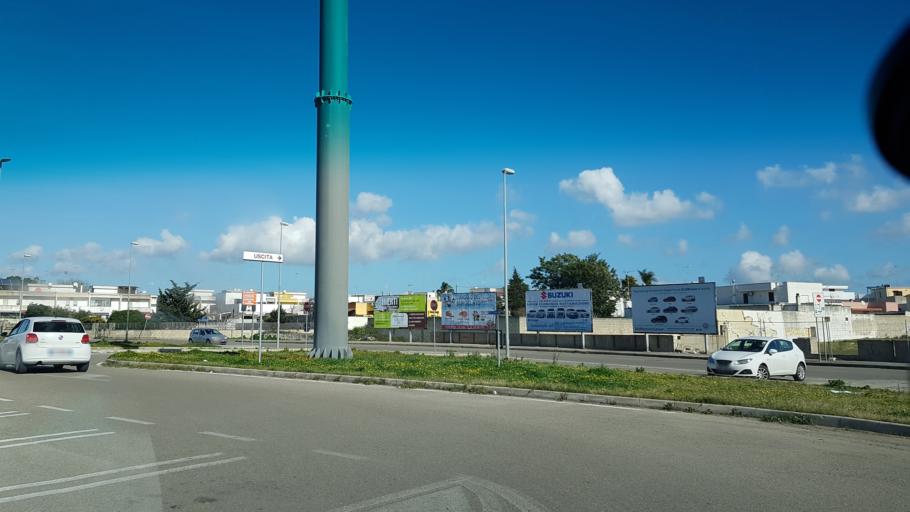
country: IT
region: Apulia
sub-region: Provincia di Lecce
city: Castromediano
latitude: 40.3247
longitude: 18.1769
